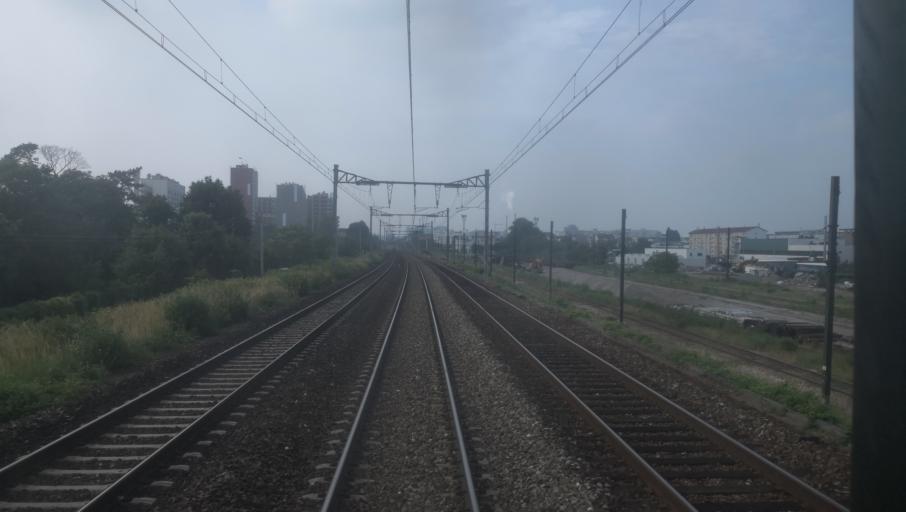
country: FR
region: Ile-de-France
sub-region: Departement du Val-de-Marne
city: Ivry-sur-Seine
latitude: 48.8076
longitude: 2.3987
